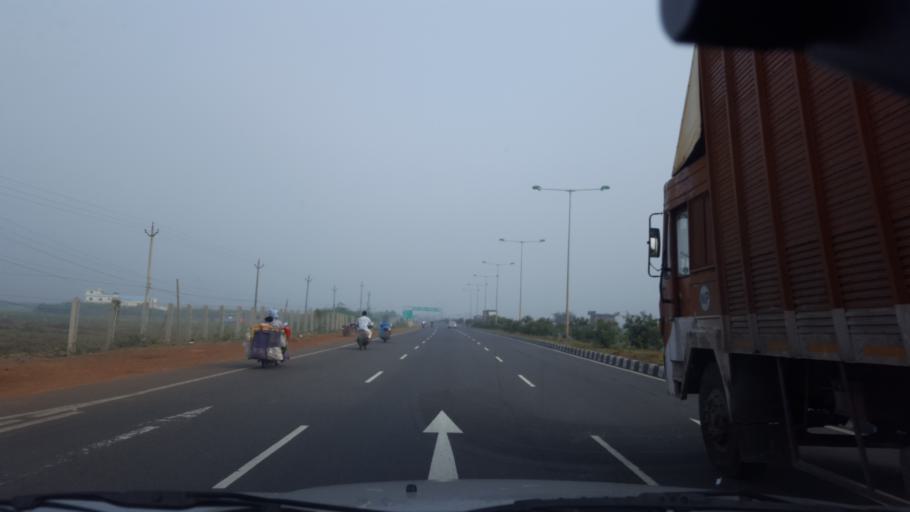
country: IN
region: Andhra Pradesh
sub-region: Prakasam
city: Ongole
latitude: 15.4625
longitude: 80.0482
